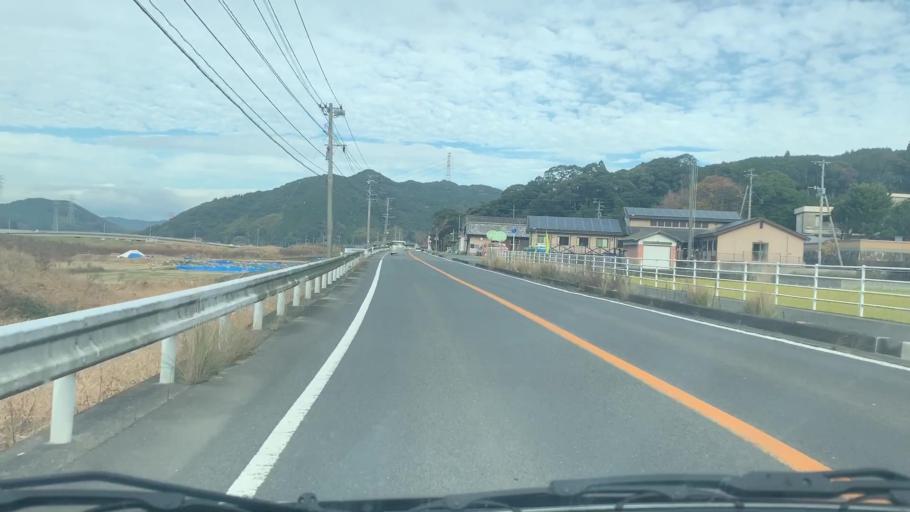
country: JP
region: Saga Prefecture
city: Karatsu
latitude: 33.3704
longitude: 130.0036
